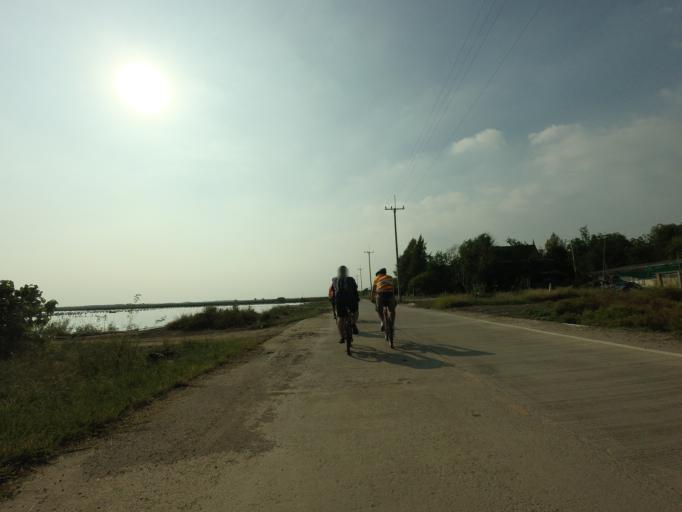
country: TH
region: Samut Sakhon
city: Samut Sakhon
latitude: 13.4987
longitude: 100.3551
